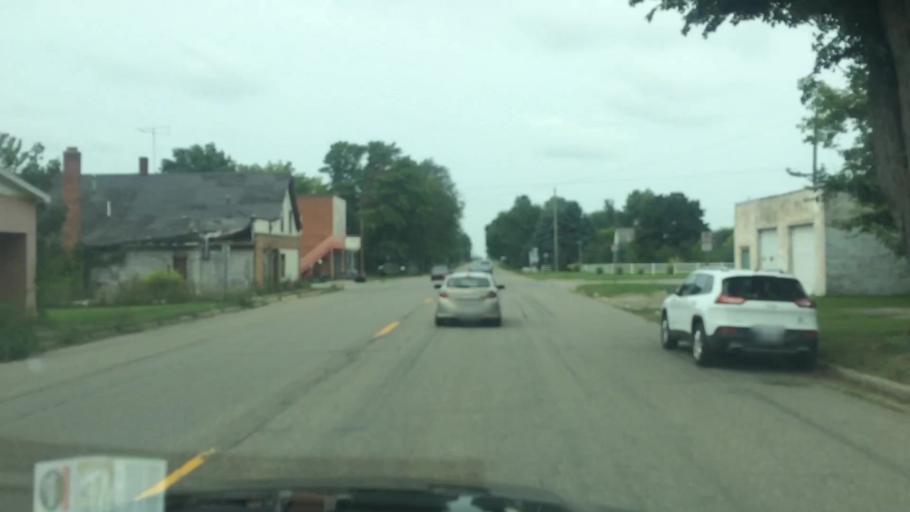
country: US
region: Michigan
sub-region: Huron County
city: Bad Axe
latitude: 43.8949
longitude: -83.0034
